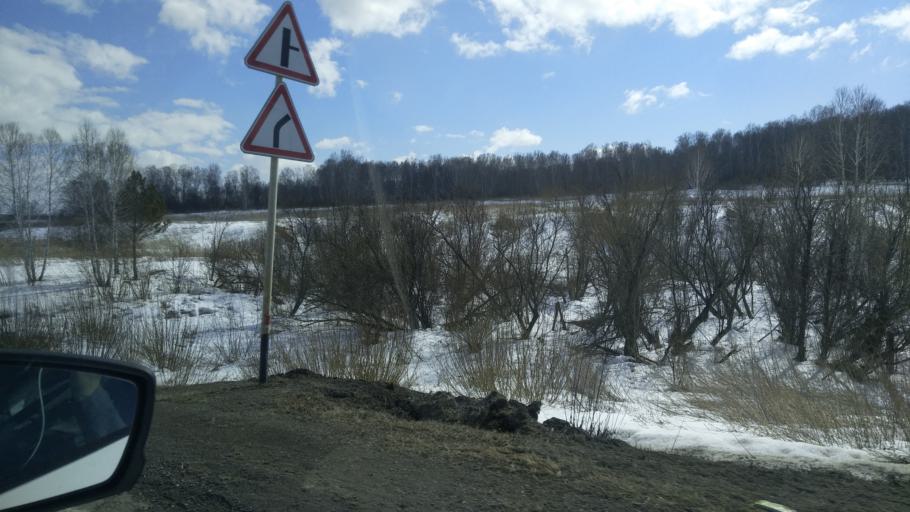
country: RU
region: Kemerovo
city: Yurga
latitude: 55.6730
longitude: 85.1527
